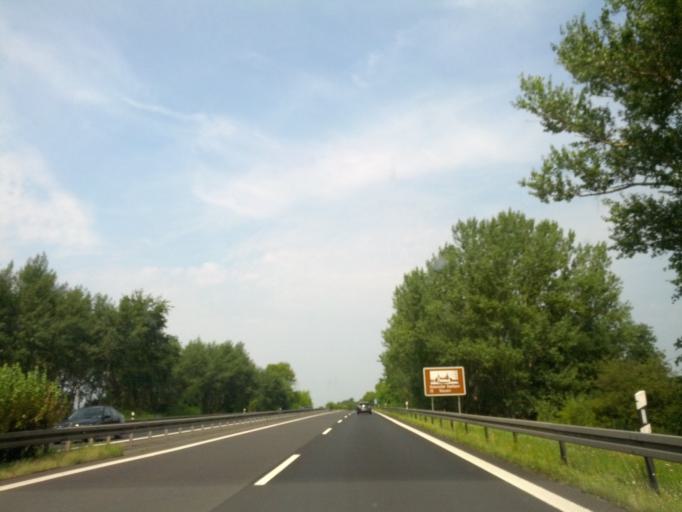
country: DE
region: Brandenburg
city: Wustermark
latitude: 52.5161
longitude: 12.9620
